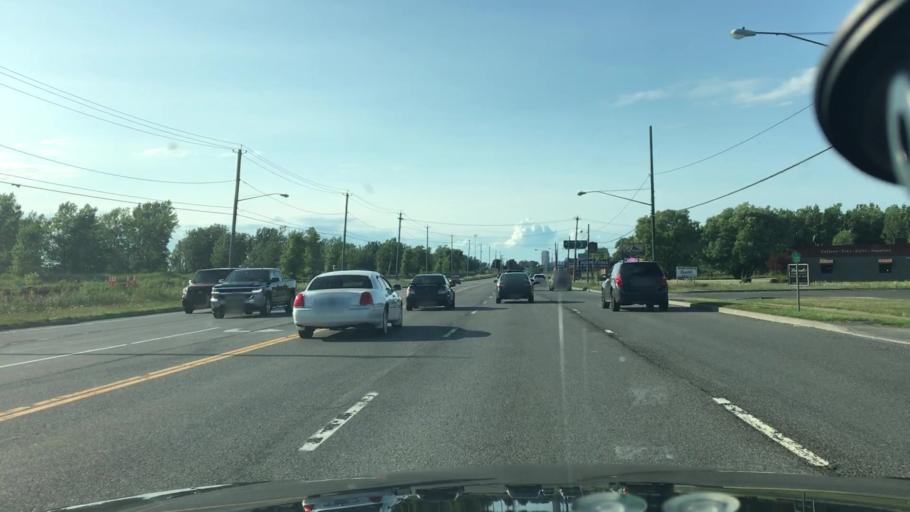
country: US
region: New York
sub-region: Erie County
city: Lackawanna
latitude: 42.8161
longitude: -78.8461
